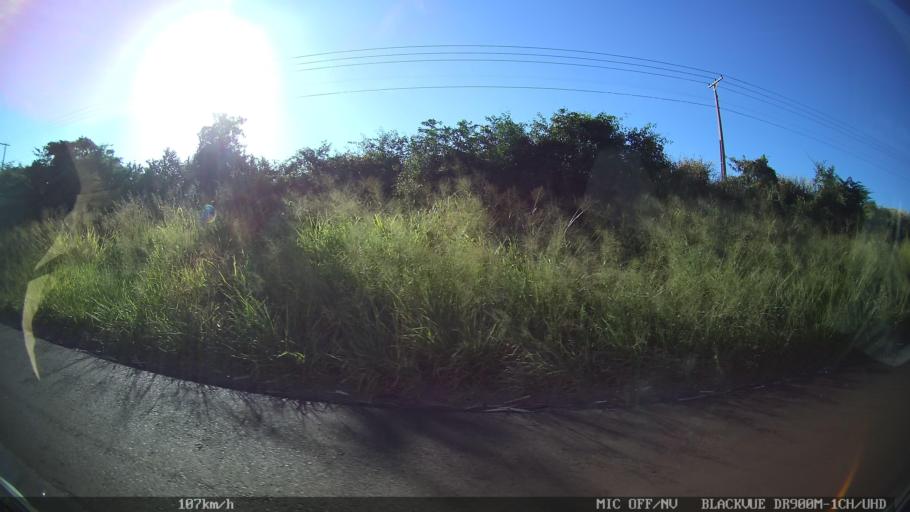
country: BR
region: Sao Paulo
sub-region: Olimpia
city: Olimpia
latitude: -20.7274
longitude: -49.0430
